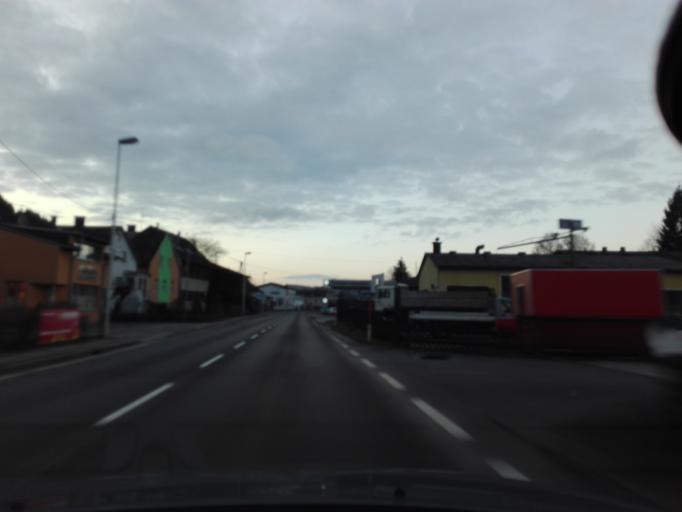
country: AT
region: Upper Austria
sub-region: Politischer Bezirk Perg
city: Bad Kreuzen
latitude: 48.2204
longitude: 14.8530
